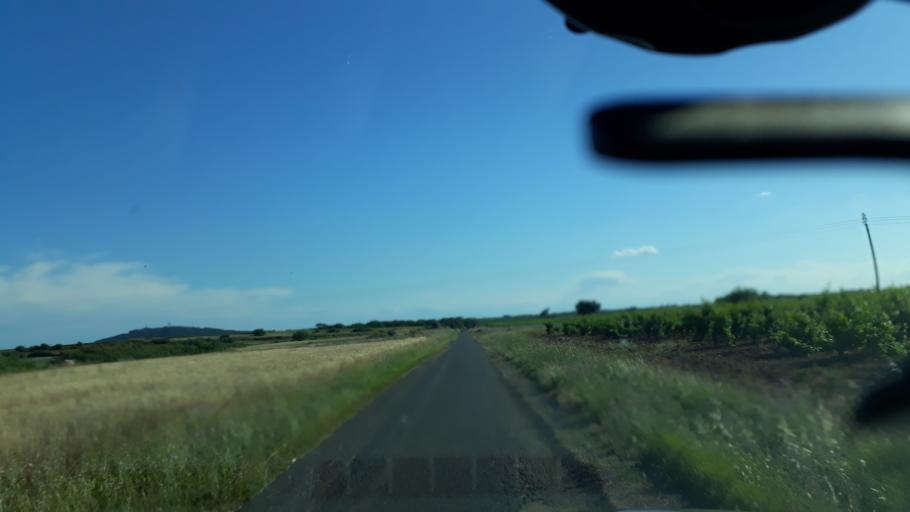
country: FR
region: Languedoc-Roussillon
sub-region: Departement de l'Herault
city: Marseillan
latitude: 43.3434
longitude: 3.5118
